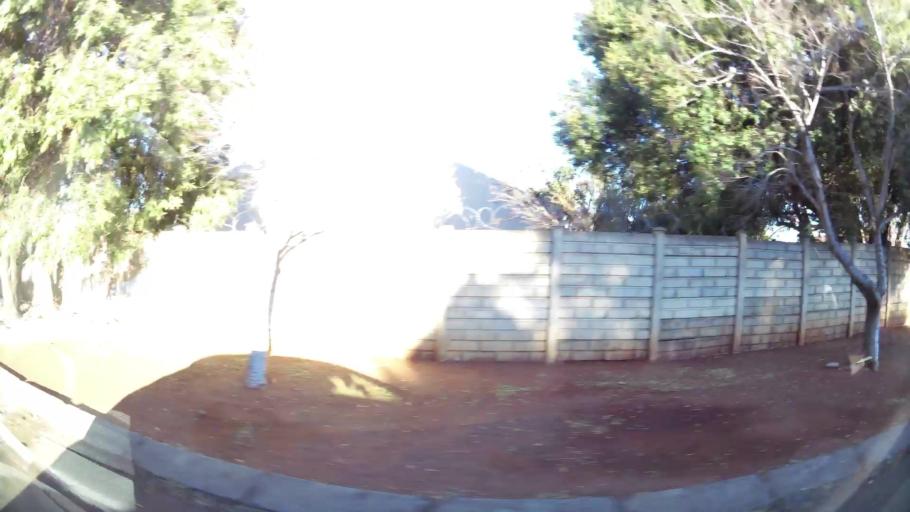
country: ZA
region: Northern Cape
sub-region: Frances Baard District Municipality
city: Kimberley
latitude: -28.7568
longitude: 24.7557
